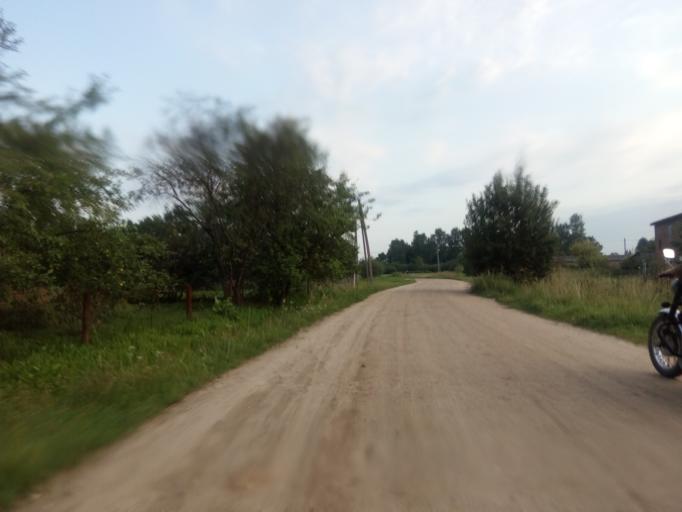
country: BY
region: Vitebsk
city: Dzisna
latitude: 55.6721
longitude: 28.3293
